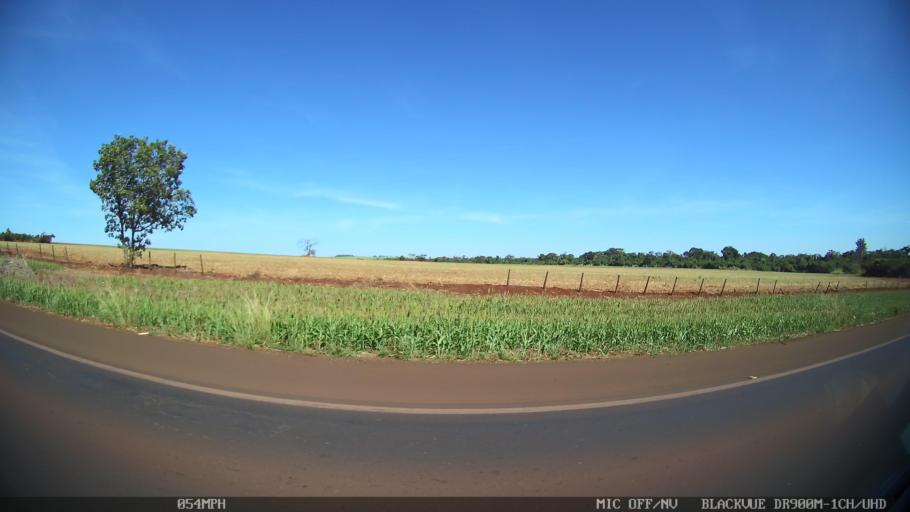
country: BR
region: Sao Paulo
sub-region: Sao Joaquim Da Barra
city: Sao Joaquim da Barra
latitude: -20.5062
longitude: -47.9277
